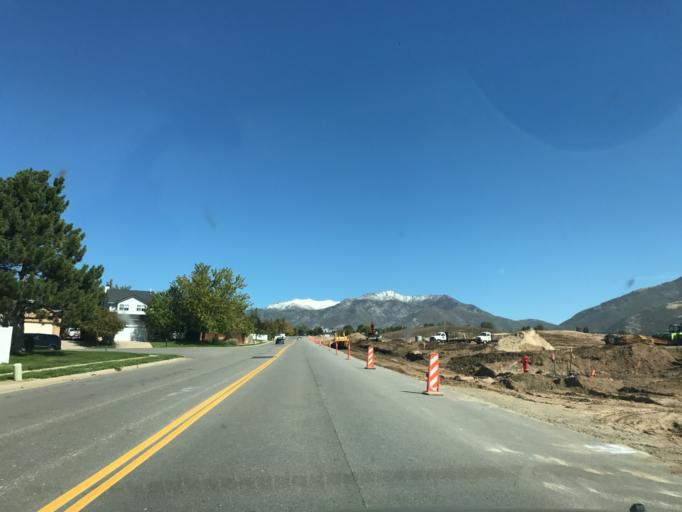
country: US
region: Utah
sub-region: Davis County
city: Hill Air Force Bace
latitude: 41.0920
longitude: -111.9428
